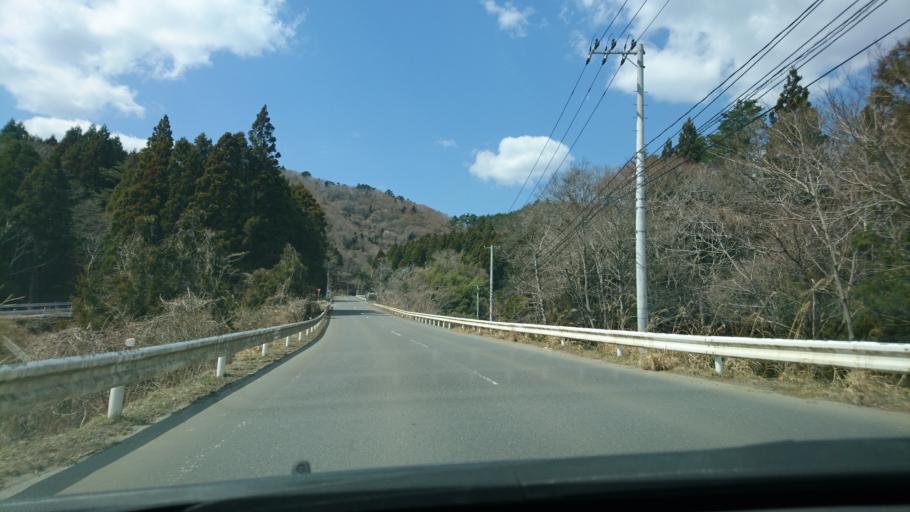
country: JP
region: Miyagi
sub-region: Oshika Gun
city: Onagawa Cho
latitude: 38.4535
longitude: 141.4902
